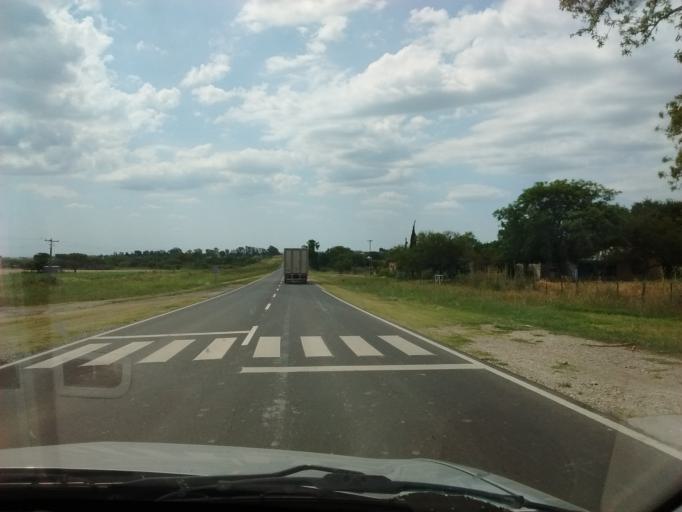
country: AR
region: Entre Rios
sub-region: Departamento de Victoria
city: Victoria
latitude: -32.7623
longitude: -59.9318
